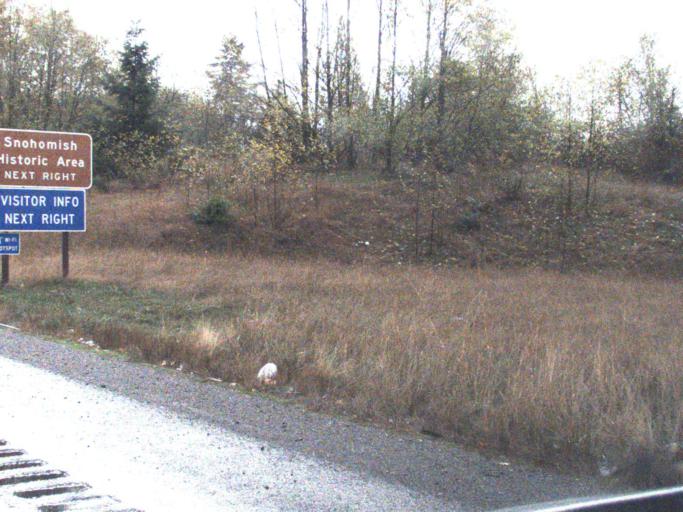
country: US
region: Washington
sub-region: Snohomish County
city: Fobes Hill
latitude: 47.9532
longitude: -122.1106
